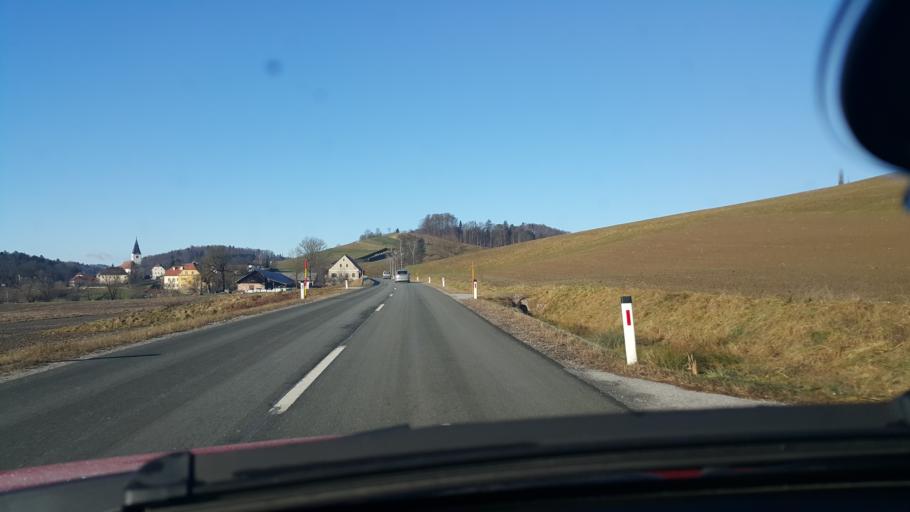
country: SI
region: Kungota
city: Zgornja Kungota
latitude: 46.6453
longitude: 15.5752
